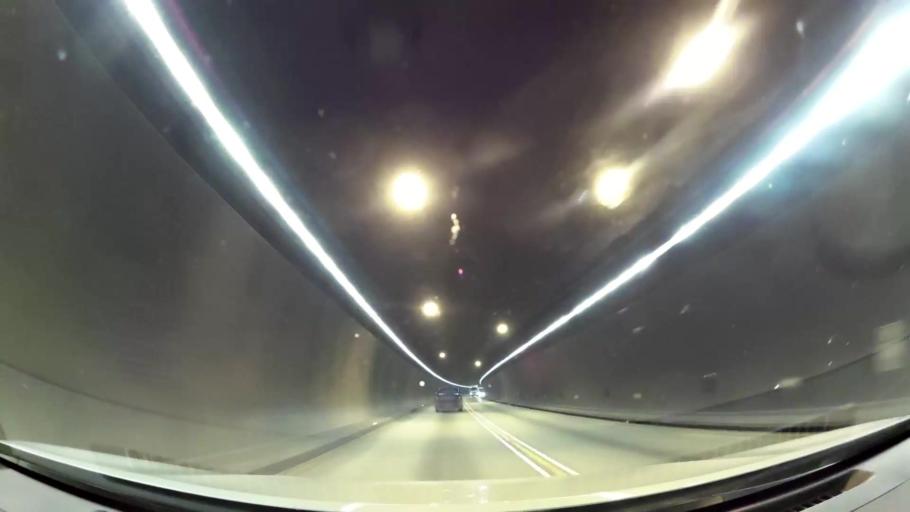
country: ZA
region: Western Cape
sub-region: Cape Winelands District Municipality
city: Paarl
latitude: -33.7335
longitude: 19.1130
